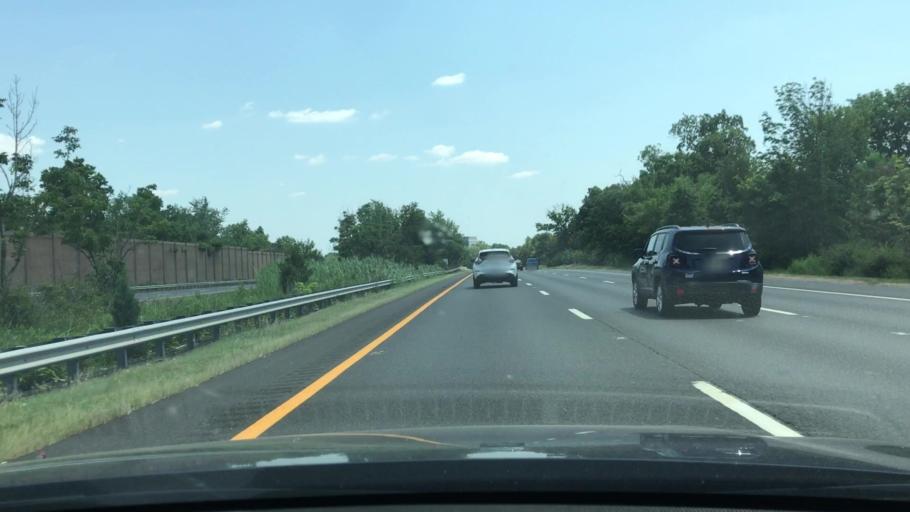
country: US
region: New Jersey
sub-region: Somerset County
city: Green Knoll
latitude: 40.5915
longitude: -74.6204
